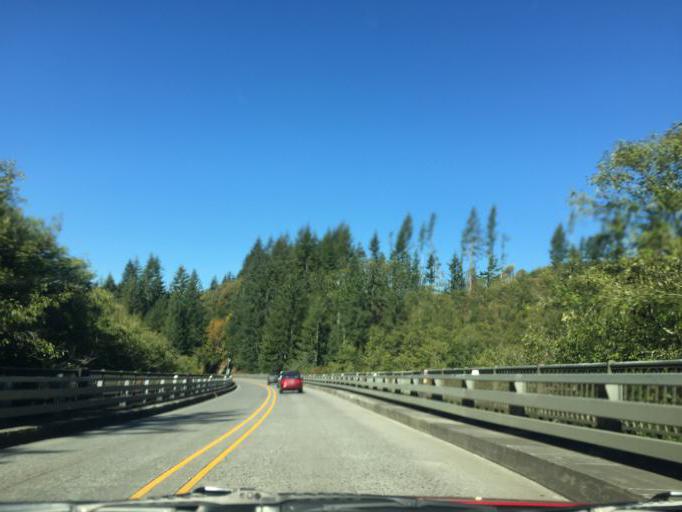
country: US
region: Oregon
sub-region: Columbia County
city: Vernonia
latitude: 45.8406
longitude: -123.5169
